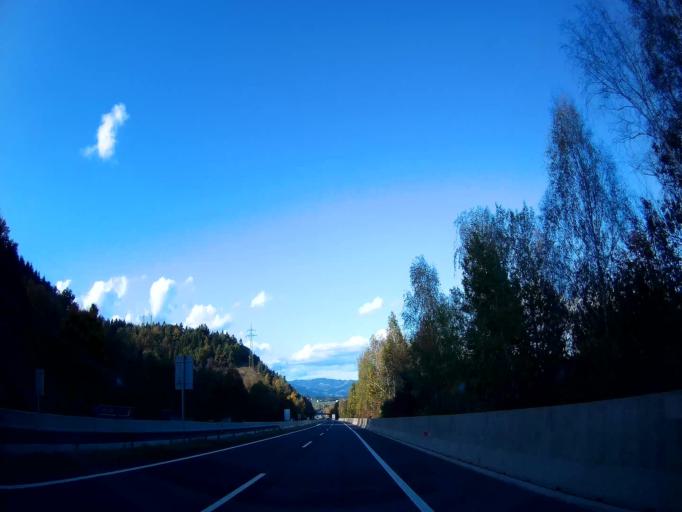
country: AT
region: Carinthia
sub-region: Politischer Bezirk Wolfsberg
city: Sankt Andrae
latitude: 46.7577
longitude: 14.8158
